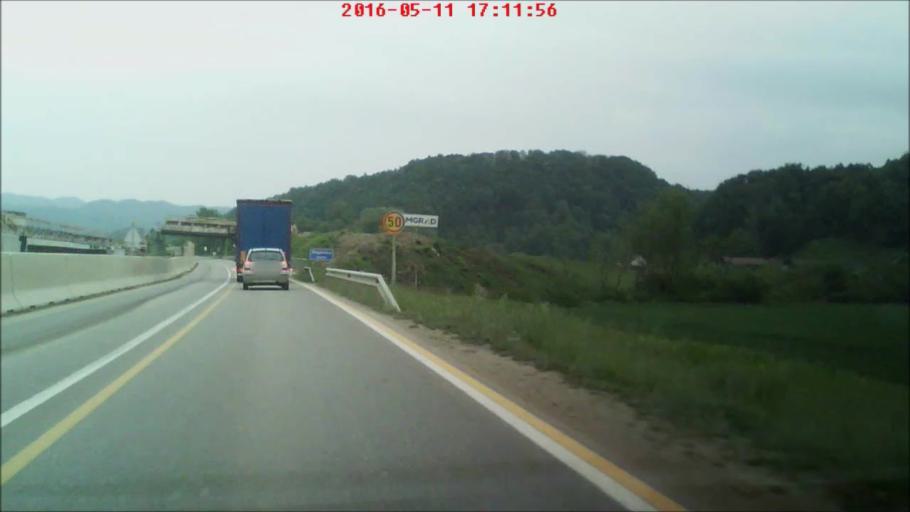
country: SI
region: Podlehnik
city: Podlehnik
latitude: 46.3515
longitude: 15.8685
